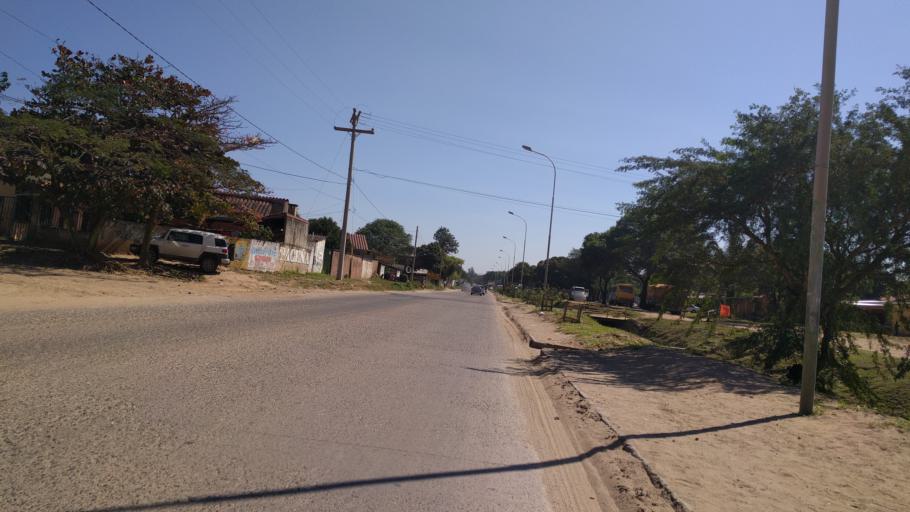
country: BO
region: Santa Cruz
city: Santa Cruz de la Sierra
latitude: -17.8278
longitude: -63.2326
